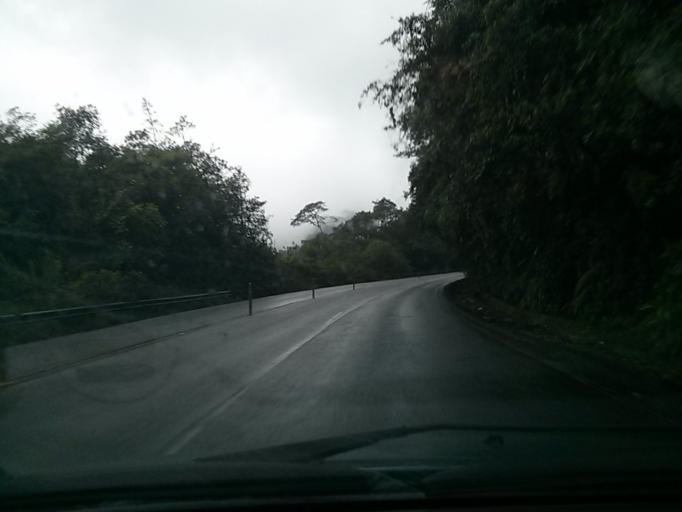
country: CR
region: San Jose
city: Dulce Nombre de Jesus
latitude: 10.0689
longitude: -83.9945
